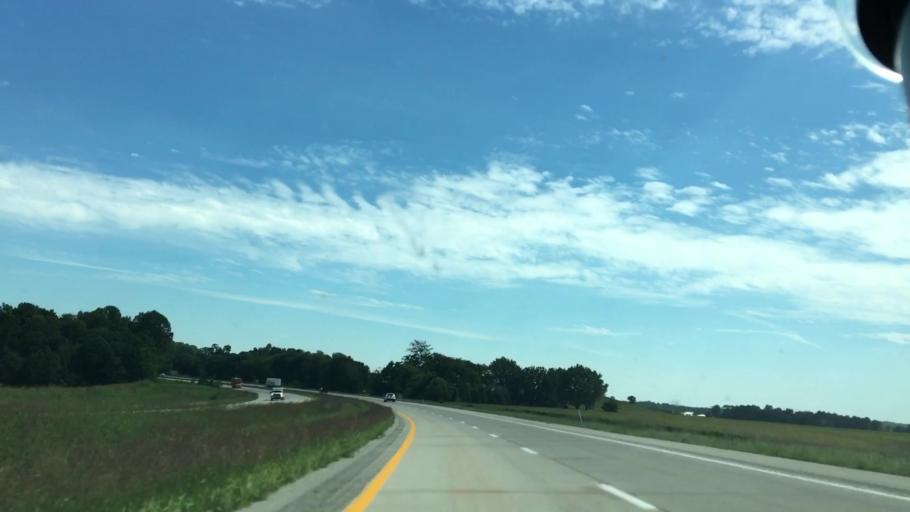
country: US
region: Kentucky
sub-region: Daviess County
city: Owensboro
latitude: 37.7528
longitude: -87.2926
